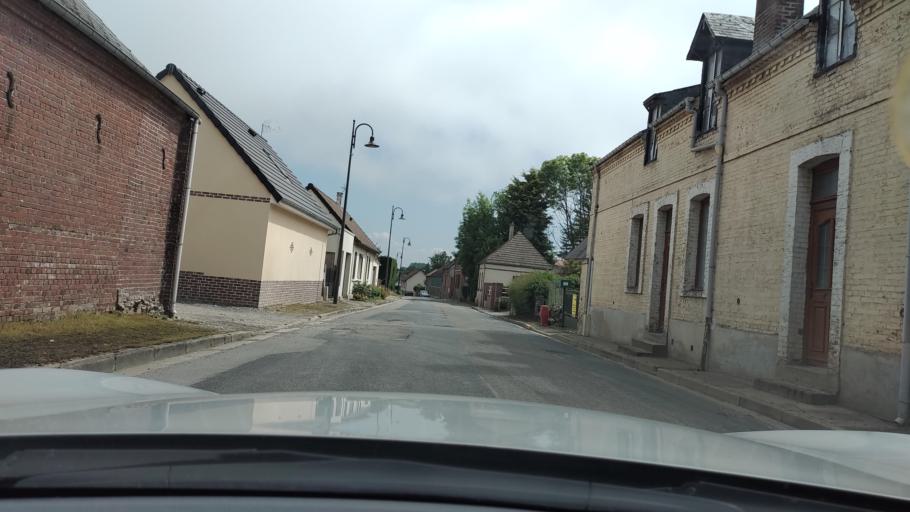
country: FR
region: Picardie
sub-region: Departement de la Somme
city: Ault
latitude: 50.0767
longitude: 1.4570
